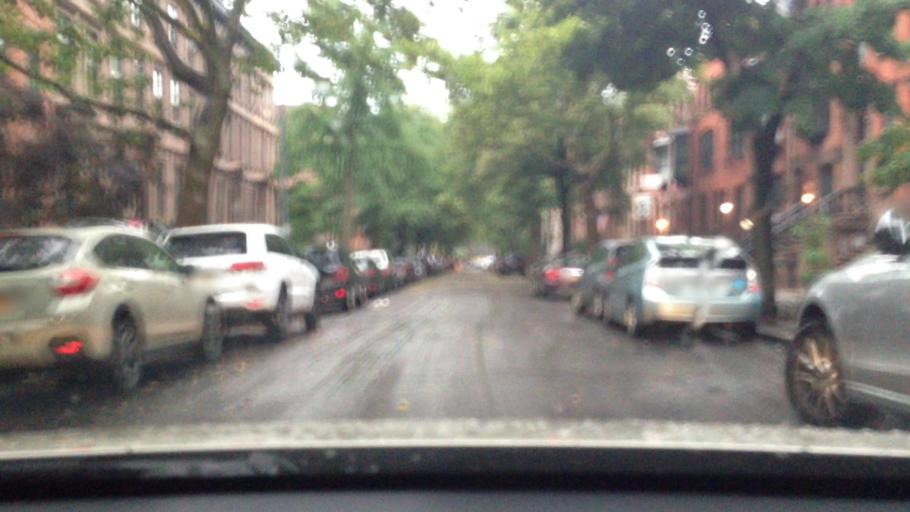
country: US
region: New York
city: New York City
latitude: 40.6849
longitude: -73.9980
